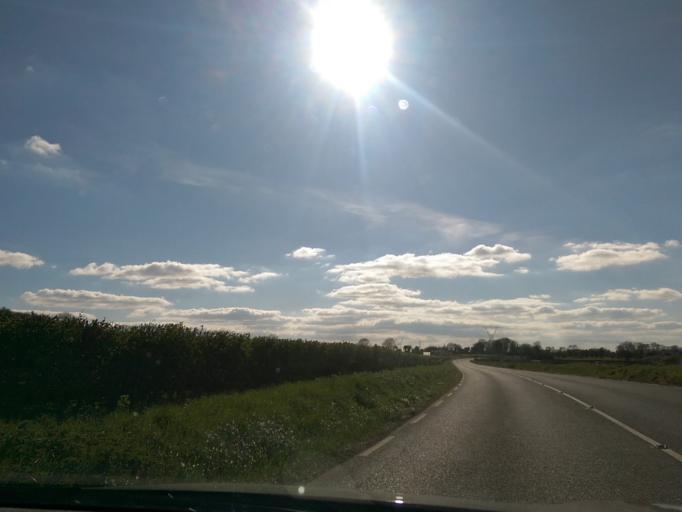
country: IE
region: Leinster
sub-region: Uibh Fhaili
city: Banagher
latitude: 53.1068
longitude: -8.0387
